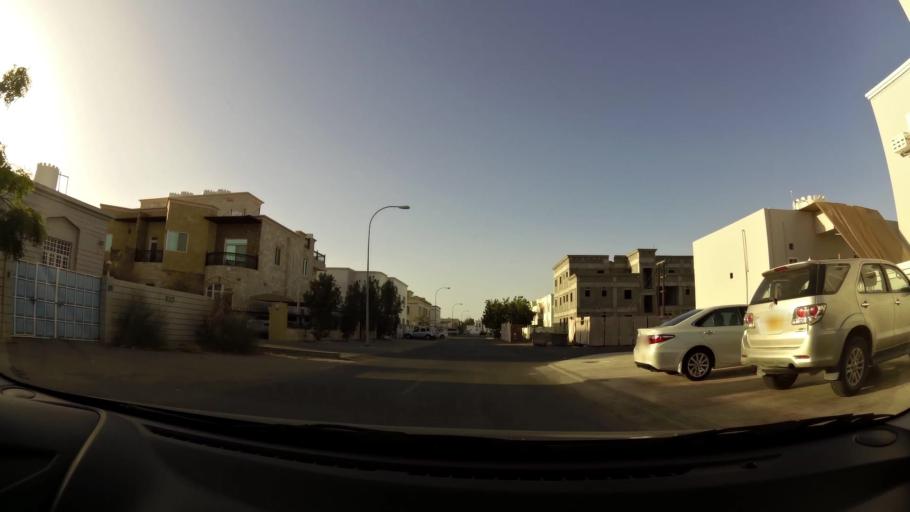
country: OM
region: Muhafazat Masqat
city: As Sib al Jadidah
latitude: 23.6105
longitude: 58.2291
